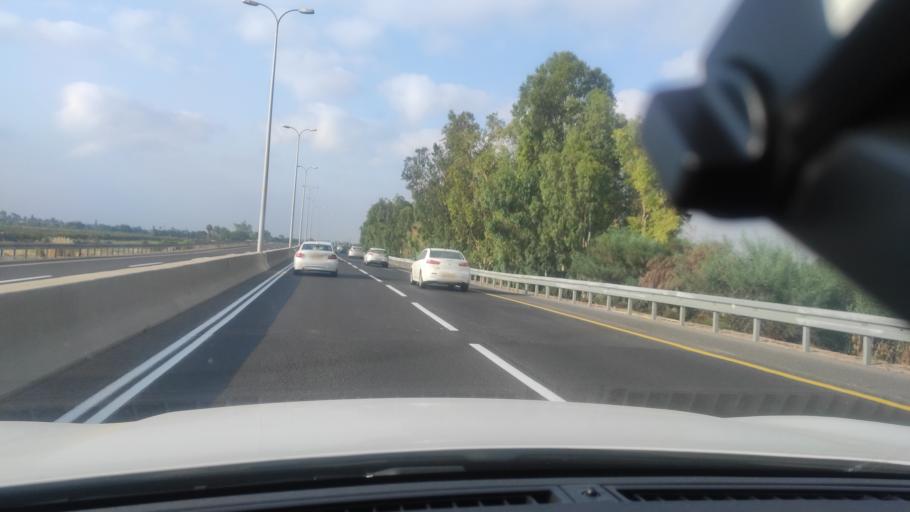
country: IL
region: Central District
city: Hod HaSharon
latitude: 32.1435
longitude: 34.9178
